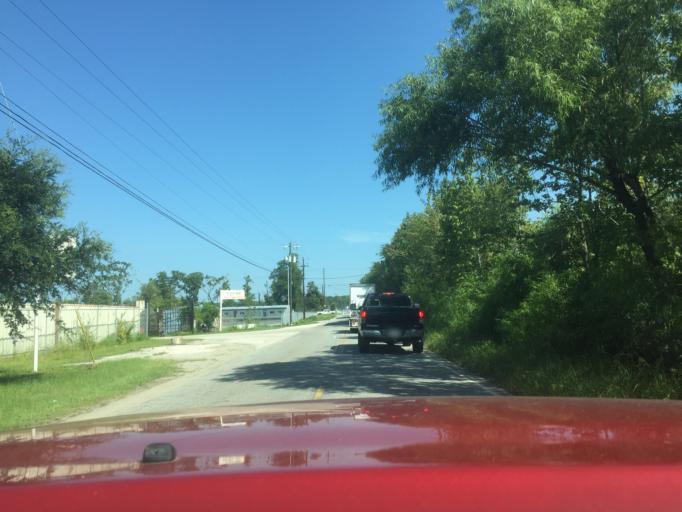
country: US
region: Georgia
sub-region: Chatham County
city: Garden City
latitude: 32.0776
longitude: -81.1451
